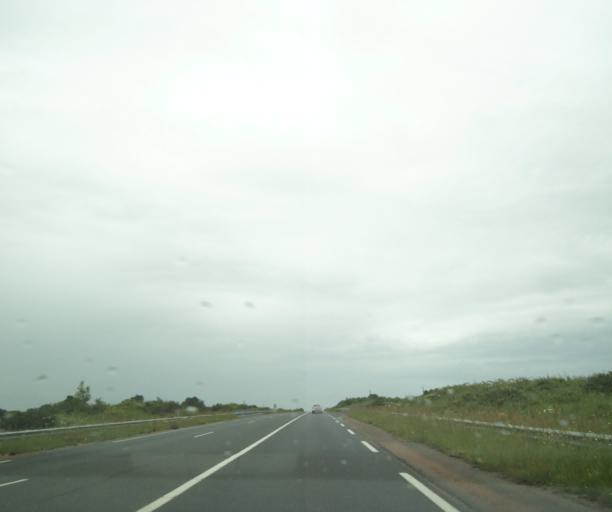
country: FR
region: Poitou-Charentes
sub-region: Departement des Deux-Sevres
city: Saint-Pardoux
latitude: 46.5165
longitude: -0.3292
